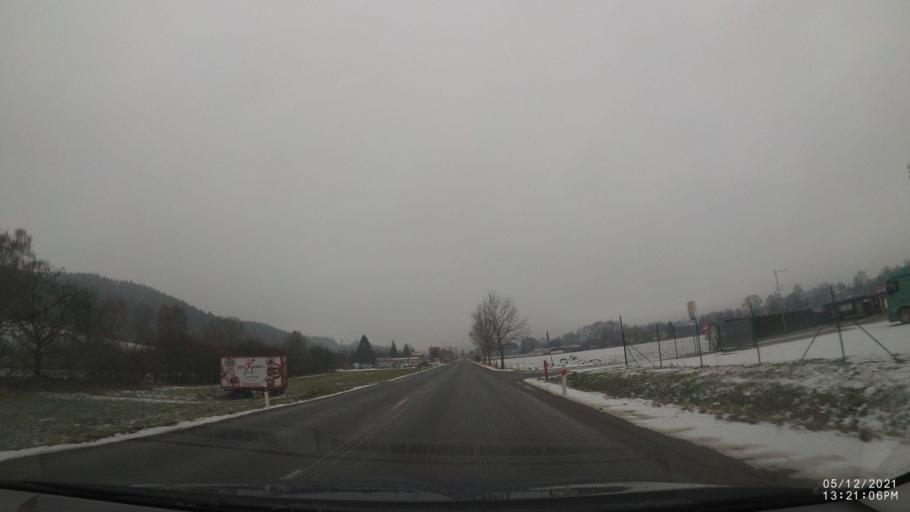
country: CZ
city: Velke Porici
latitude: 50.4551
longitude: 16.1875
